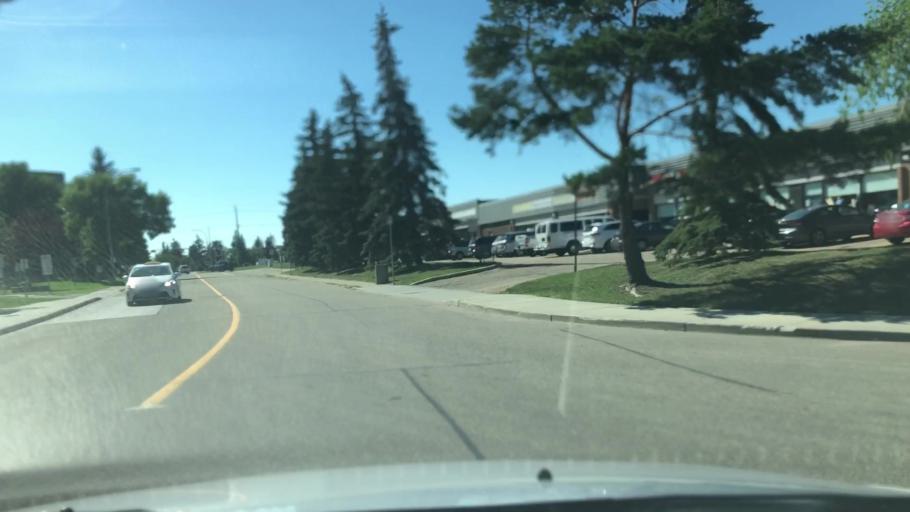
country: CA
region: Alberta
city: Edmonton
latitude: 53.5375
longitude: -113.4150
